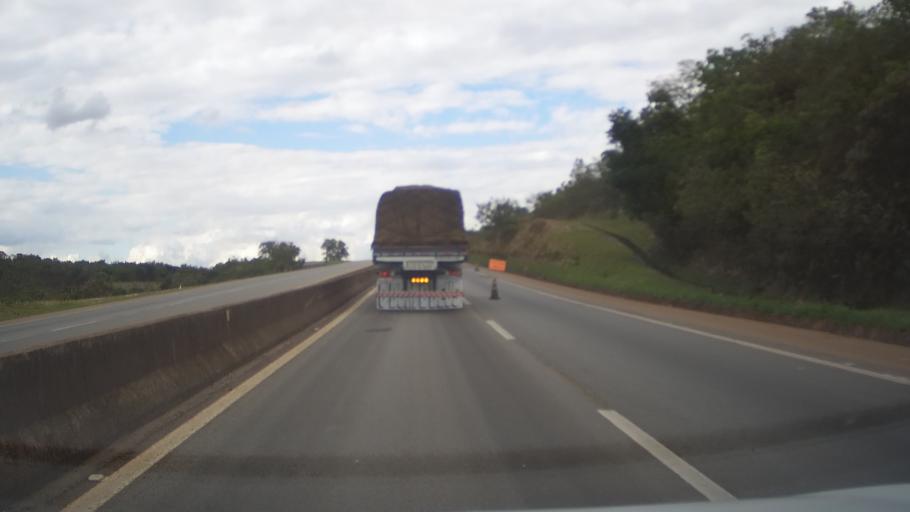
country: BR
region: Minas Gerais
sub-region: Itauna
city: Itauna
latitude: -20.3104
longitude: -44.4499
